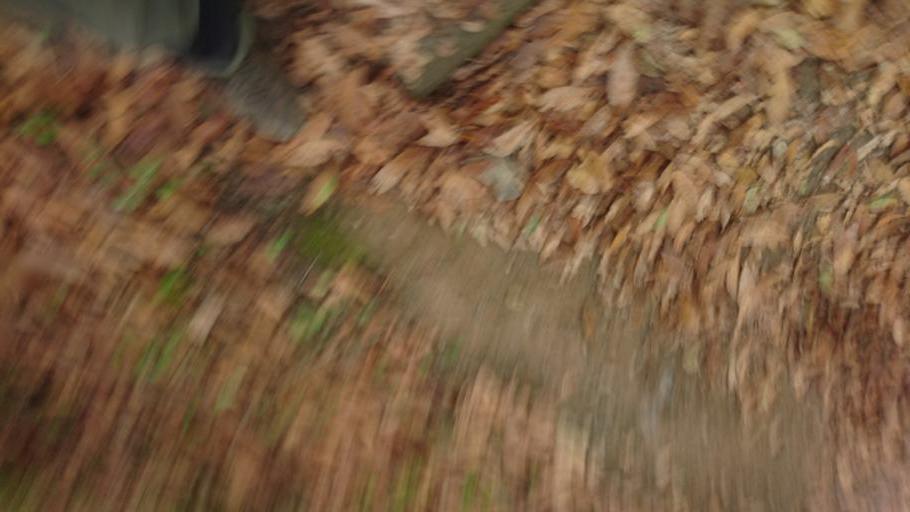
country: MX
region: Nuevo Leon
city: Garza Garcia
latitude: 25.6010
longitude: -100.3389
